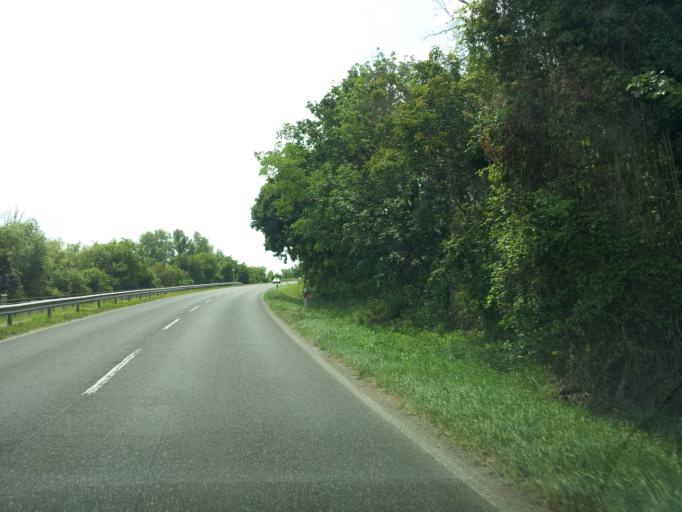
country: HU
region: Veszprem
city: Balatonalmadi
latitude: 47.0035
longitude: 18.0018
